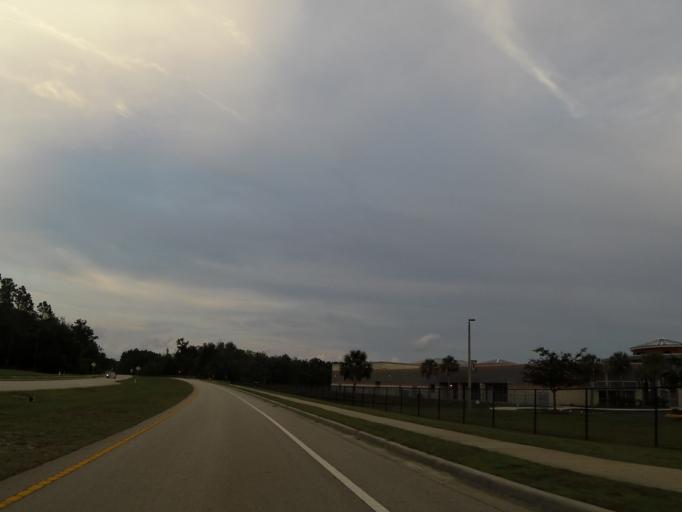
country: US
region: Florida
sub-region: Saint Johns County
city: Fruit Cove
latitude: 30.0823
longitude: -81.5635
